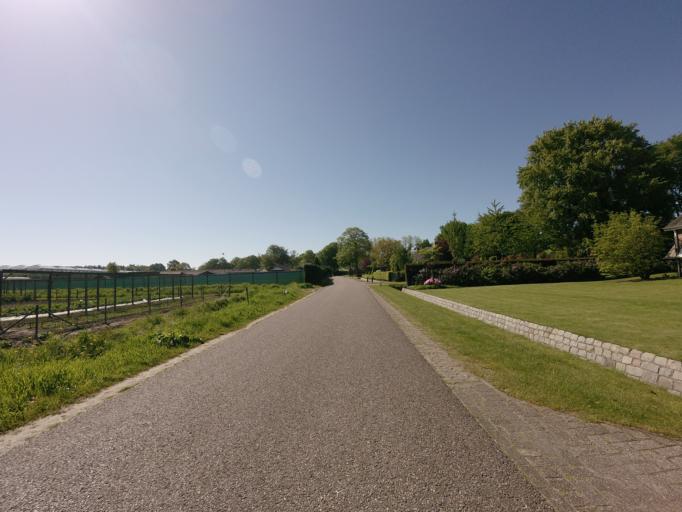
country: NL
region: North Brabant
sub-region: Gemeente Rucphen
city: Rucphen
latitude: 51.5785
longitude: 4.5577
